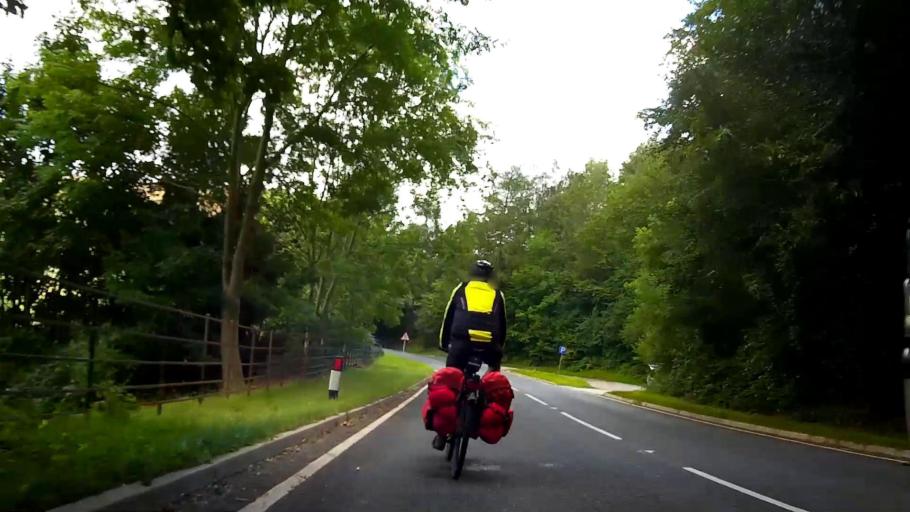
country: GB
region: Wales
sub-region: Denbighshire
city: Llangollen
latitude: 53.0065
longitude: -3.1934
